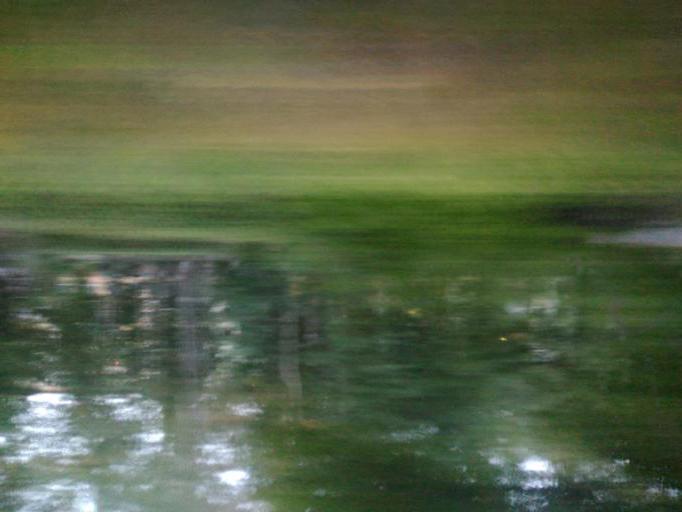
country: RU
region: Ulyanovsk
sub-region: Ulyanovskiy Rayon
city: Ulyanovsk
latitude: 54.3015
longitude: 48.3225
